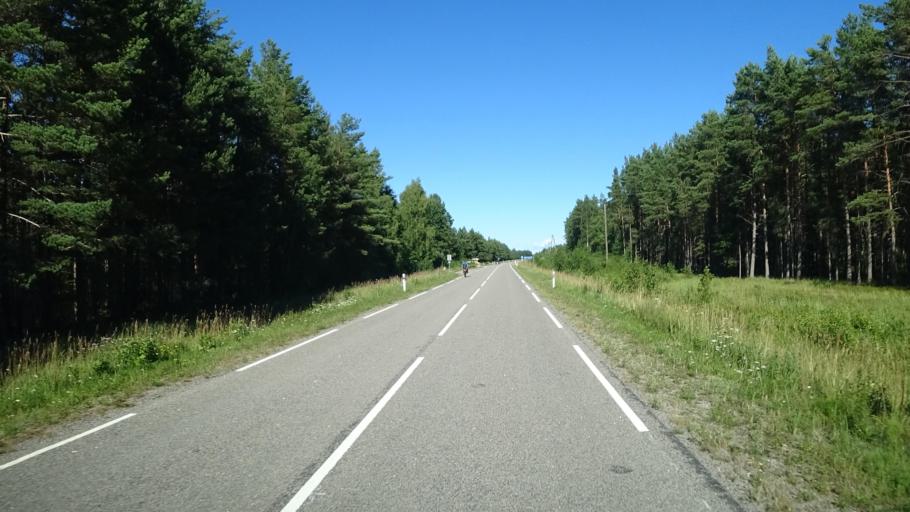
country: LV
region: Dundaga
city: Dundaga
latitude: 57.6935
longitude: 22.3945
